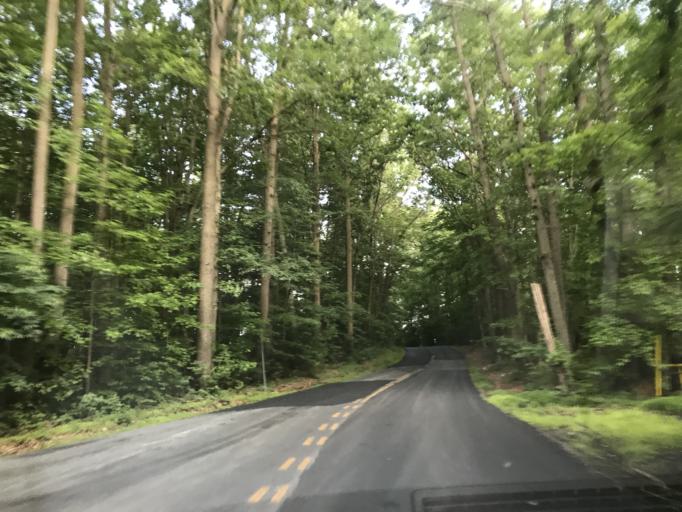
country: US
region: Maryland
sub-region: Harford County
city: Aberdeen
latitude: 39.5204
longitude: -76.2095
